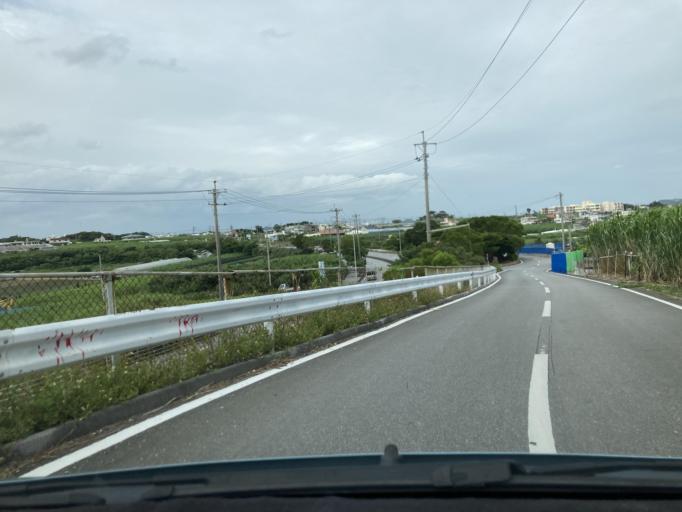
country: JP
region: Okinawa
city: Tomigusuku
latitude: 26.1575
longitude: 127.7014
